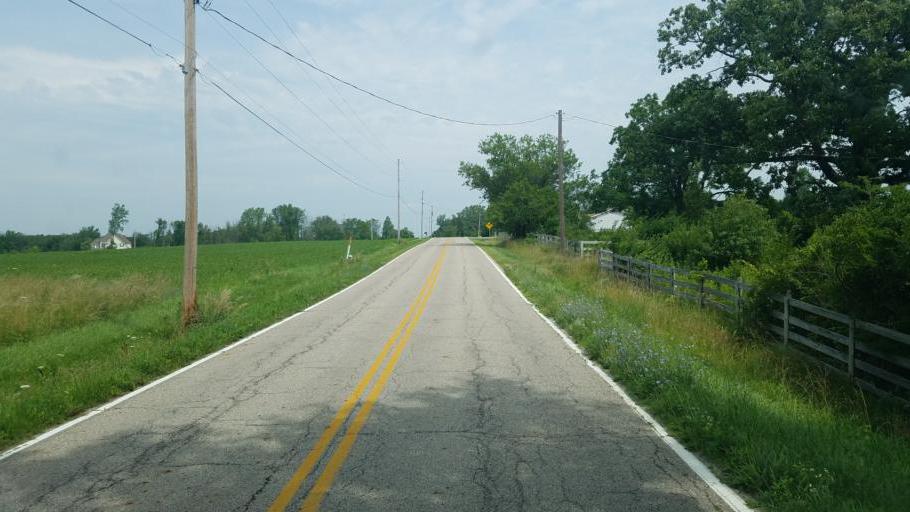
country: US
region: Ohio
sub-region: Madison County
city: West Jefferson
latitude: 39.9001
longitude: -83.2573
